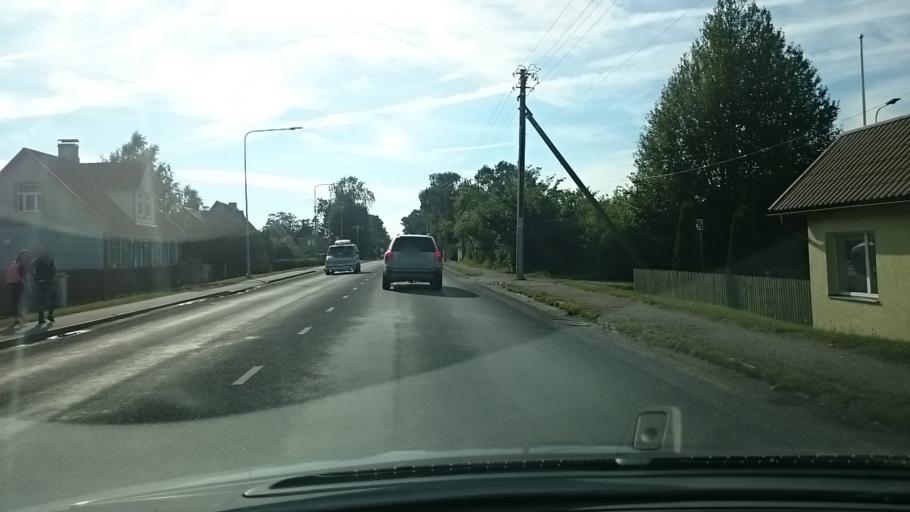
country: EE
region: Laeaene
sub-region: Haapsalu linn
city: Haapsalu
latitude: 58.9373
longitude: 23.5614
